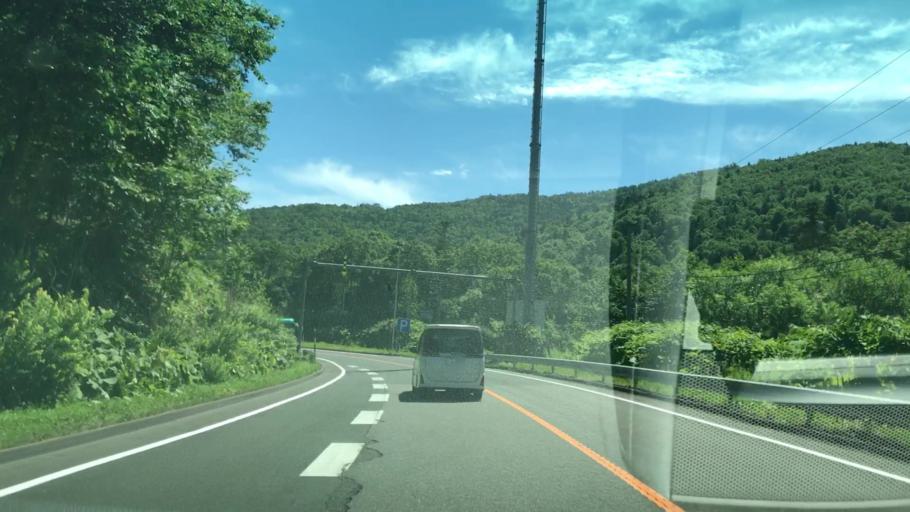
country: JP
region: Hokkaido
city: Shimo-furano
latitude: 42.9629
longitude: 142.6544
